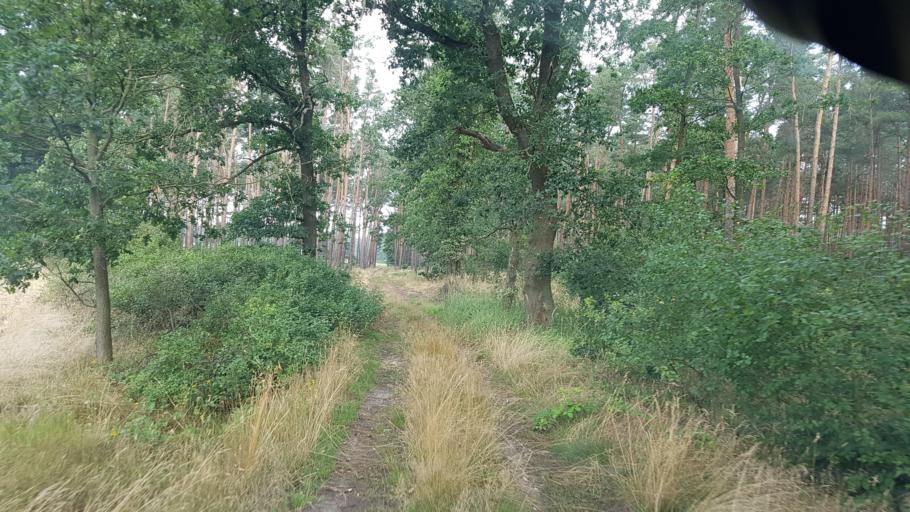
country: DE
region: Brandenburg
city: Schonborn
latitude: 51.6805
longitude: 13.4897
